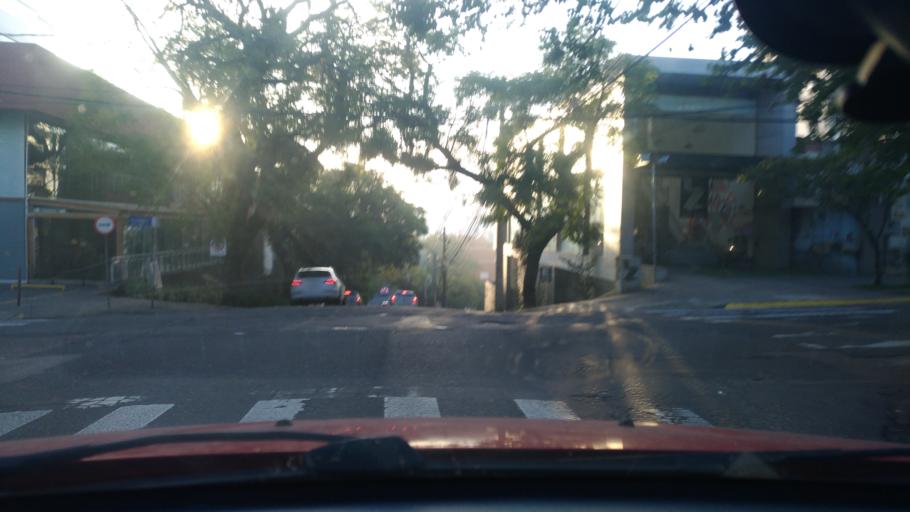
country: BR
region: Rio Grande do Sul
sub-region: Porto Alegre
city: Porto Alegre
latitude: -30.0272
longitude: -51.1934
